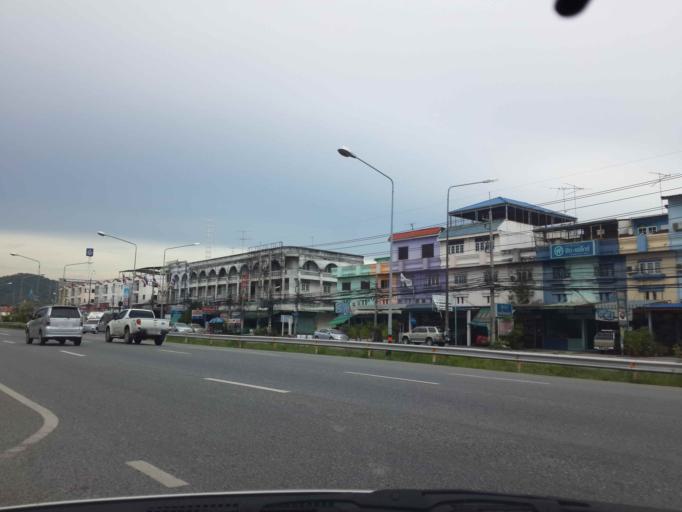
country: TH
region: Chon Buri
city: Si Racha
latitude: 13.2206
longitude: 100.9406
